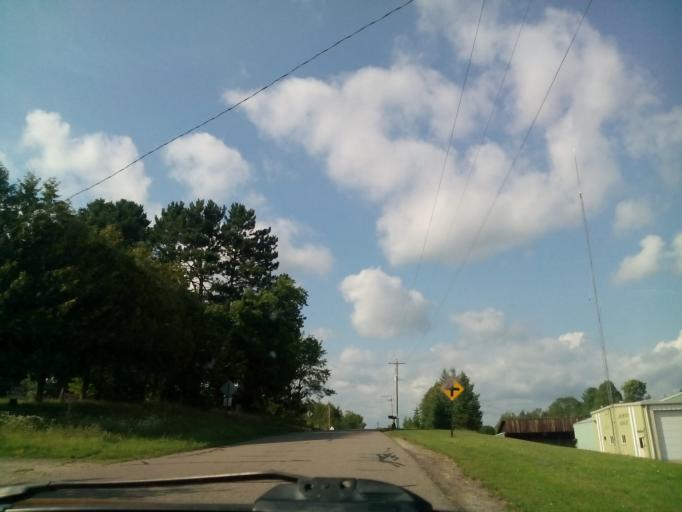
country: US
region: Wisconsin
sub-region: Menominee County
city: Legend Lake
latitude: 45.3071
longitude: -88.5221
